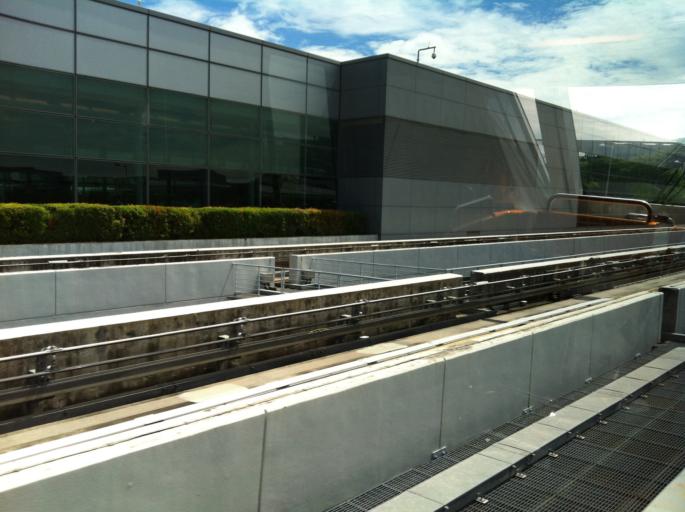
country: SG
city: Singapore
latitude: 1.3531
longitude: 103.9851
